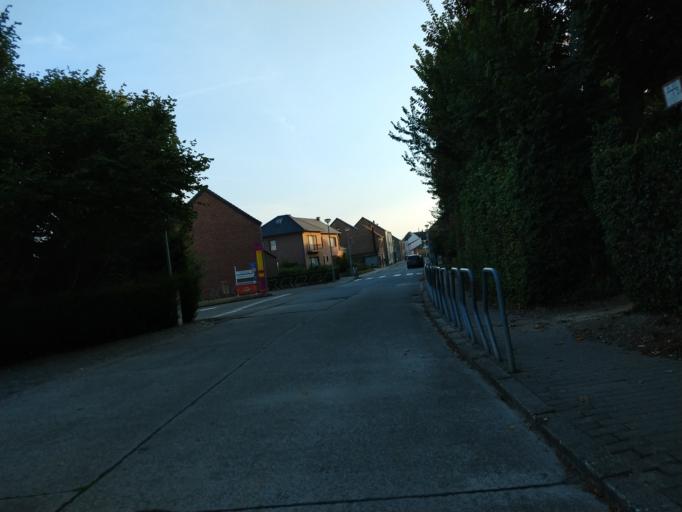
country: BE
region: Flanders
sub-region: Provincie Vlaams-Brabant
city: Hoegaarden
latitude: 50.7790
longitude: 4.8998
